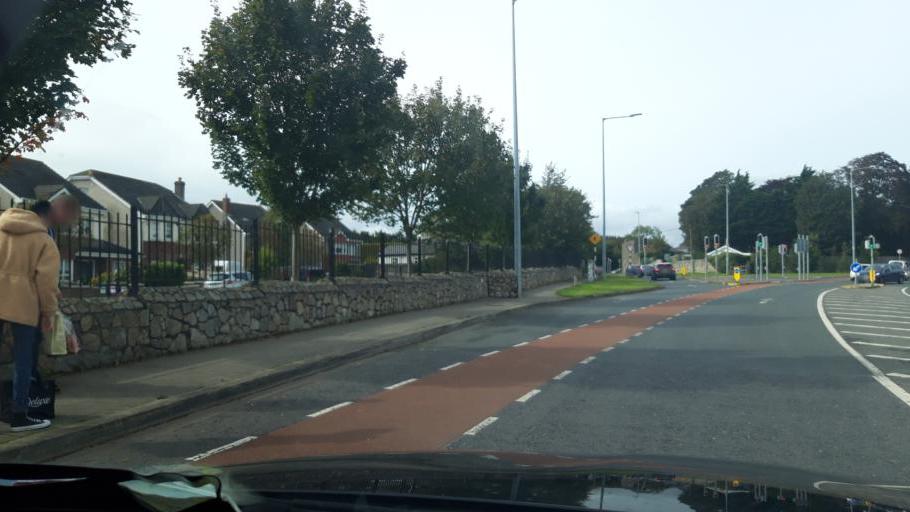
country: IE
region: Leinster
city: Sandyford
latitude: 53.2624
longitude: -6.2096
